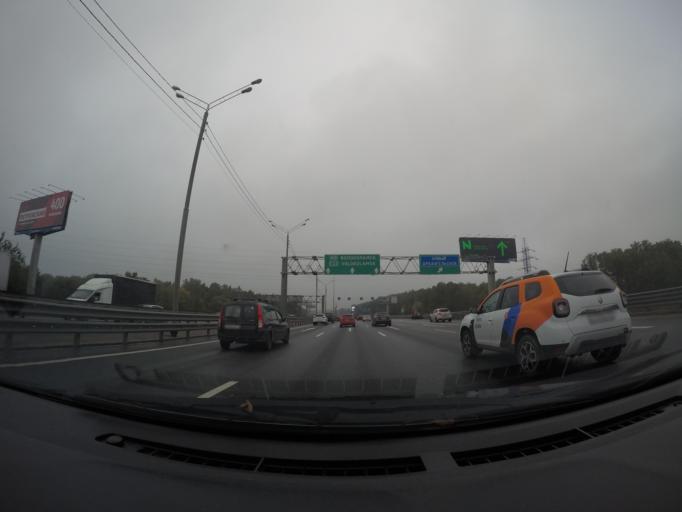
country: RU
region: Moskovskaya
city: Arkhangel'skoye
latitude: 55.8028
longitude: 37.2920
